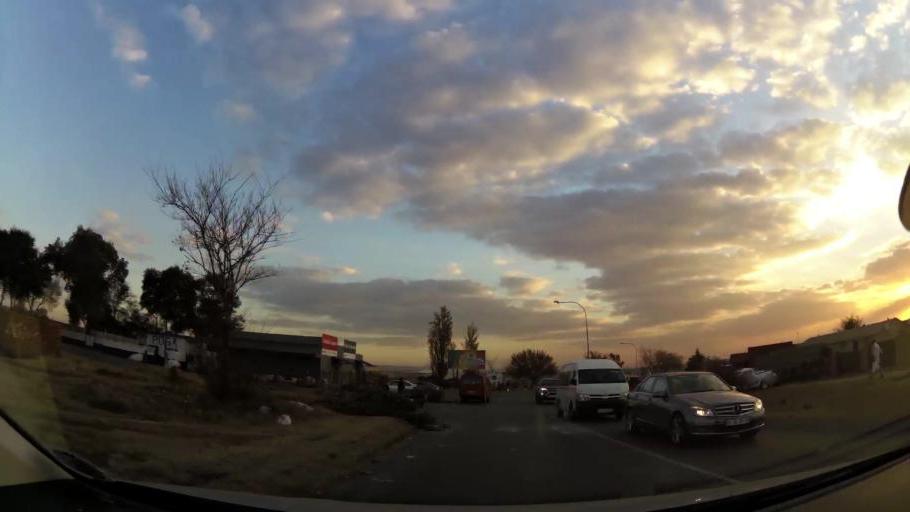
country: ZA
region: Gauteng
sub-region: City of Johannesburg Metropolitan Municipality
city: Soweto
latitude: -26.2754
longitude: 27.8987
